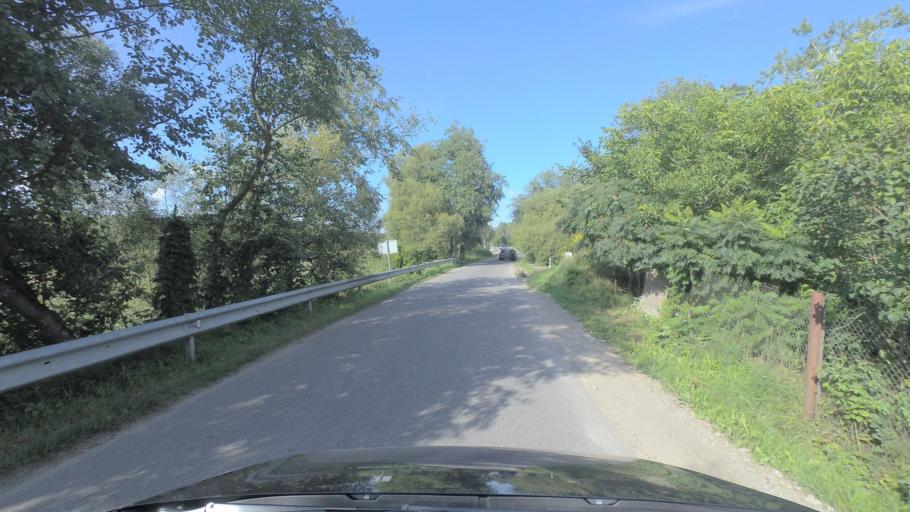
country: LT
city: Nemencine
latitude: 54.8314
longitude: 25.3665
